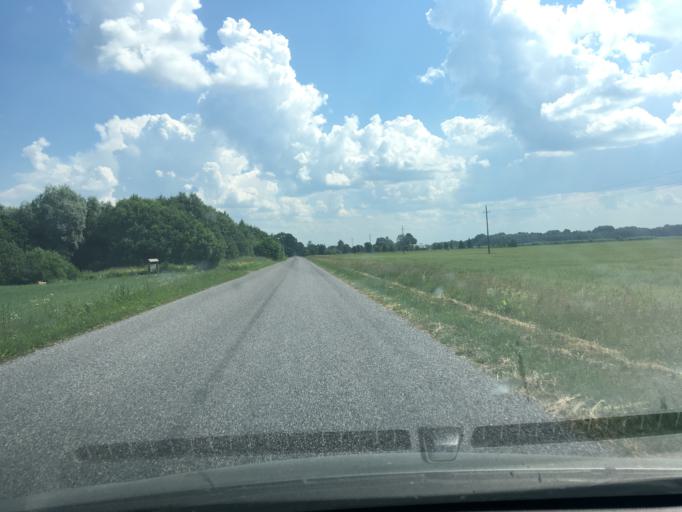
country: EE
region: Laeaene
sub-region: Lihula vald
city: Lihula
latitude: 58.7140
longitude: 24.0006
